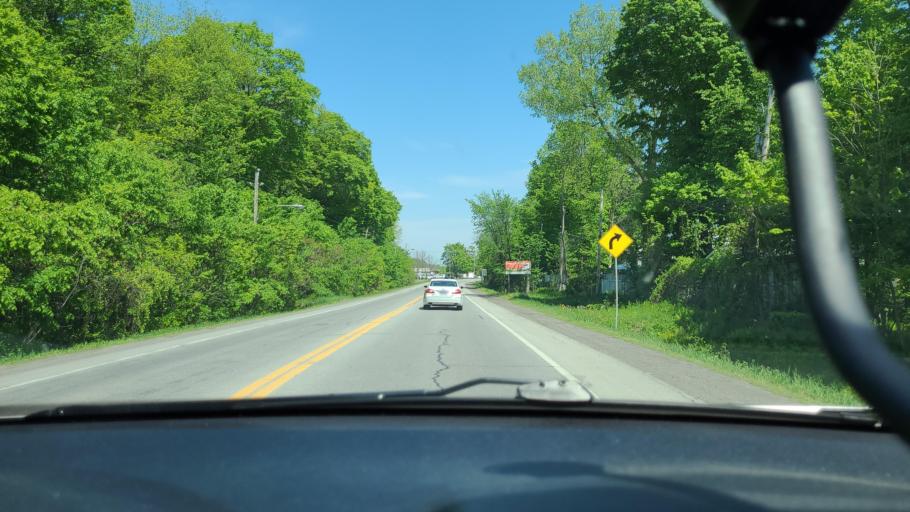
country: CA
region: Quebec
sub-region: Laurentides
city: Saint-Eustache
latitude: 45.5866
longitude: -73.9345
